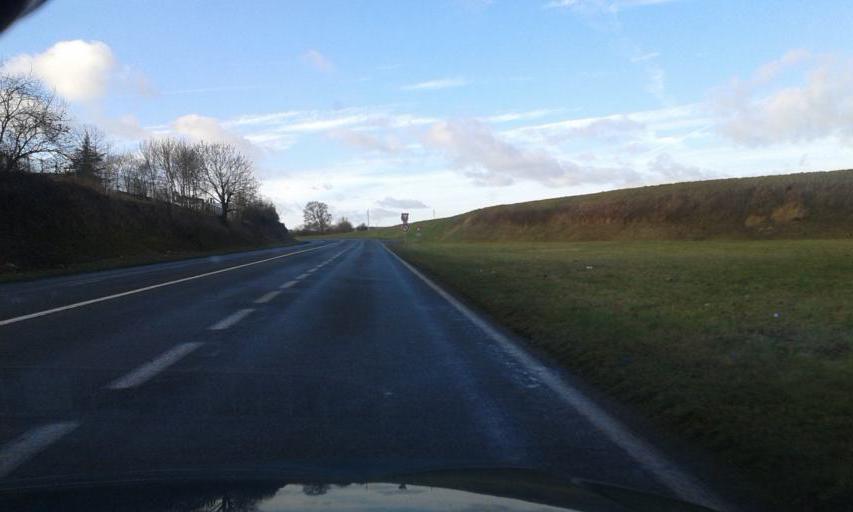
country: FR
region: Picardie
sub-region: Departement de l'Oise
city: Venette
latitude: 49.4094
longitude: 2.7859
